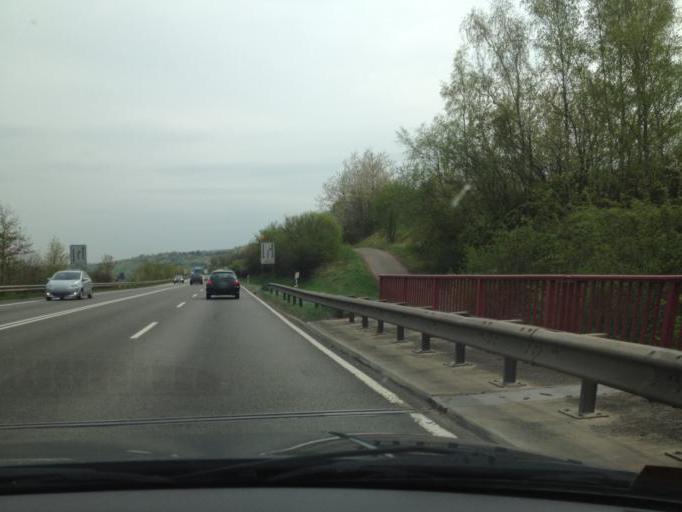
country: DE
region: Rheinland-Pfalz
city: Albersweiler
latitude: 49.2129
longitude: 8.0273
